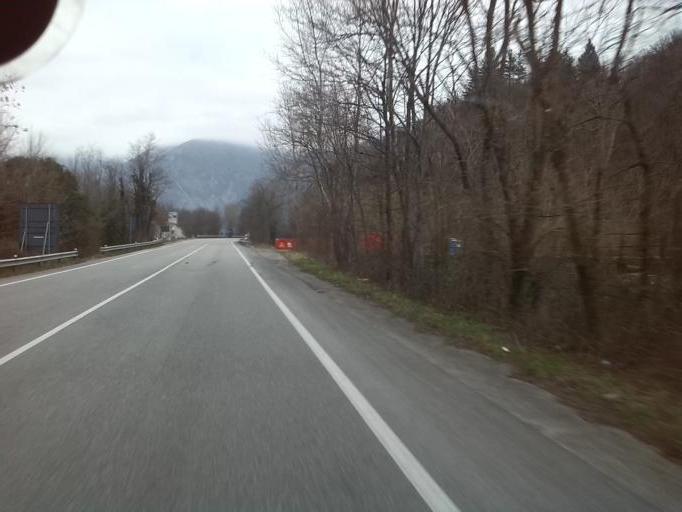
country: IT
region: Friuli Venezia Giulia
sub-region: Provincia di Udine
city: Bordano
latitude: 46.3038
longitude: 13.1214
